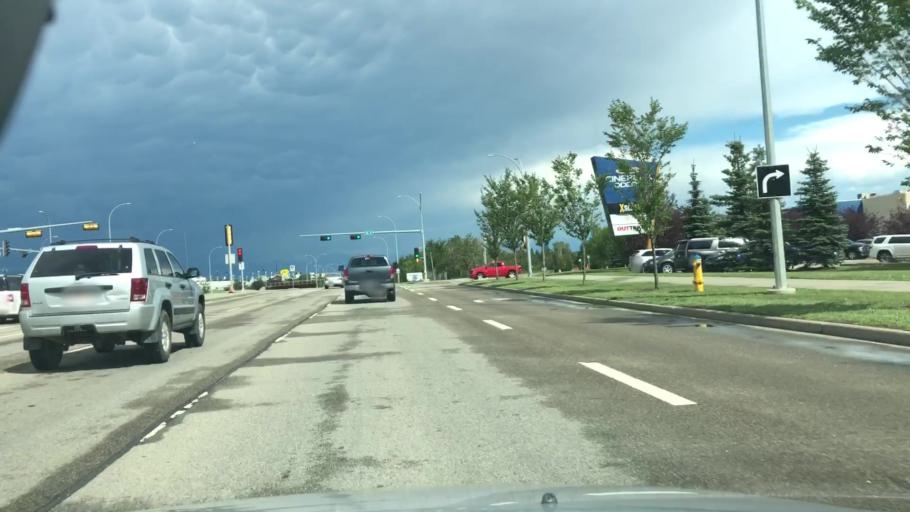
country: CA
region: Alberta
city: St. Albert
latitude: 53.5993
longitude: -113.5700
